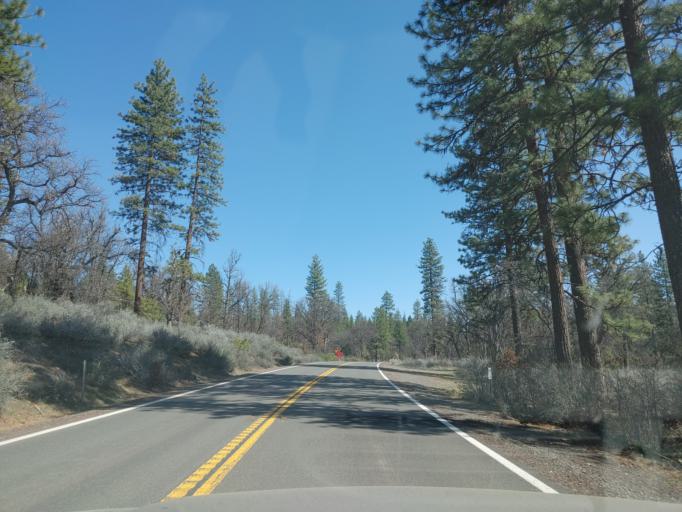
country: US
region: California
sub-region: Shasta County
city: Burney
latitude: 41.0075
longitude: -121.6361
